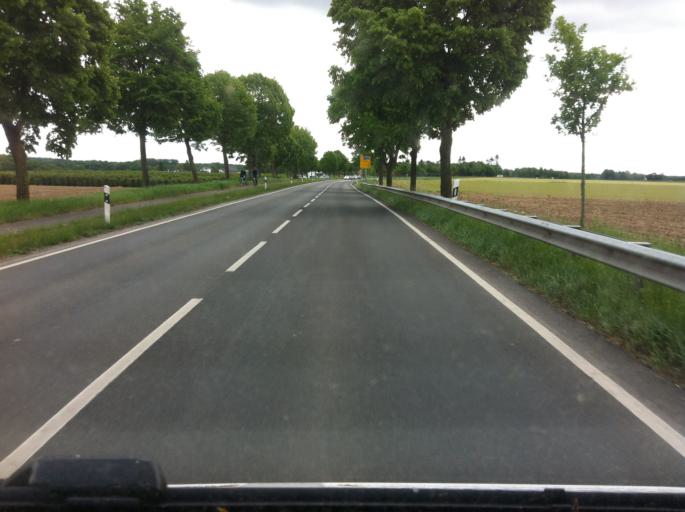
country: DE
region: North Rhine-Westphalia
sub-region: Regierungsbezirk Dusseldorf
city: Niederkruchten
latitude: 51.2225
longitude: 6.2031
